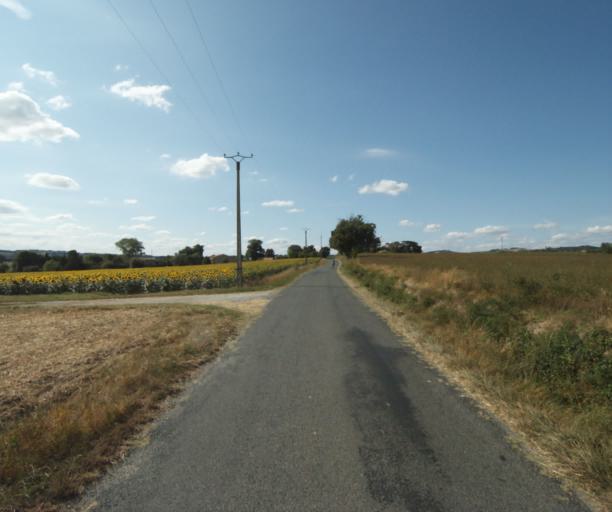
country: FR
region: Midi-Pyrenees
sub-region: Departement du Tarn
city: Puylaurens
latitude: 43.5292
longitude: 1.9756
